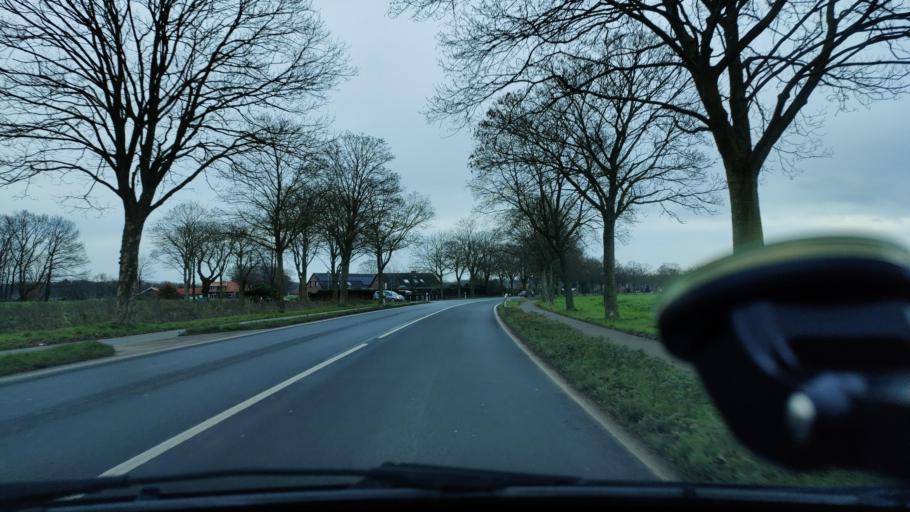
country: DE
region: North Rhine-Westphalia
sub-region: Regierungsbezirk Dusseldorf
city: Alpen
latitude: 51.5726
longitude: 6.4903
